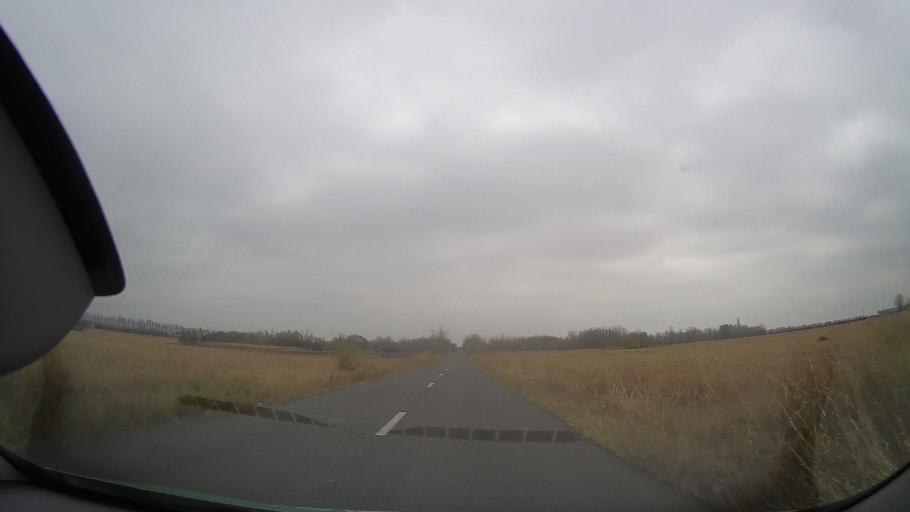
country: RO
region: Buzau
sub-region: Comuna Bradeanu
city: Bradeanu
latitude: 44.8860
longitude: 26.8754
